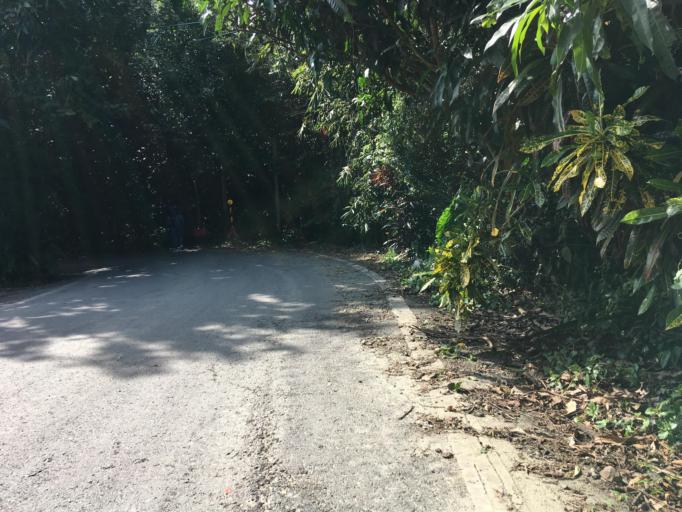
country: TW
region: Taiwan
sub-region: Yilan
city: Yilan
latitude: 24.8409
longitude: 121.7808
